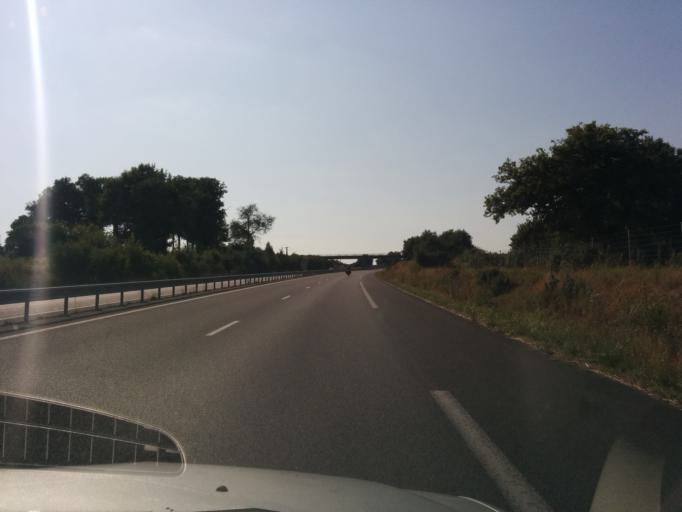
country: FR
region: Poitou-Charentes
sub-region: Departement des Deux-Sevres
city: Le Pin
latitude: 46.8998
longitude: -0.6606
